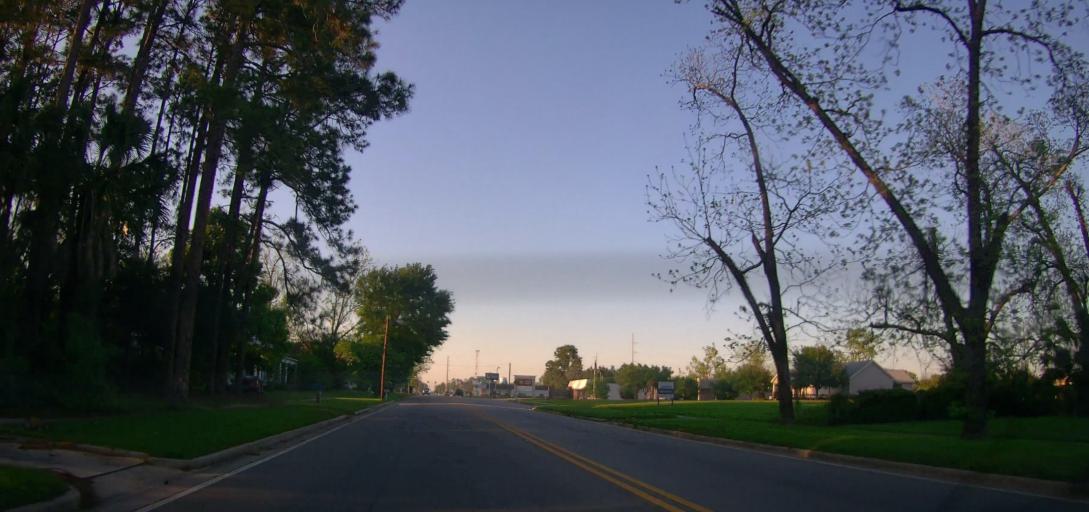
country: US
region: Georgia
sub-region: Irwin County
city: Ocilla
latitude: 31.5998
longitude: -83.2521
